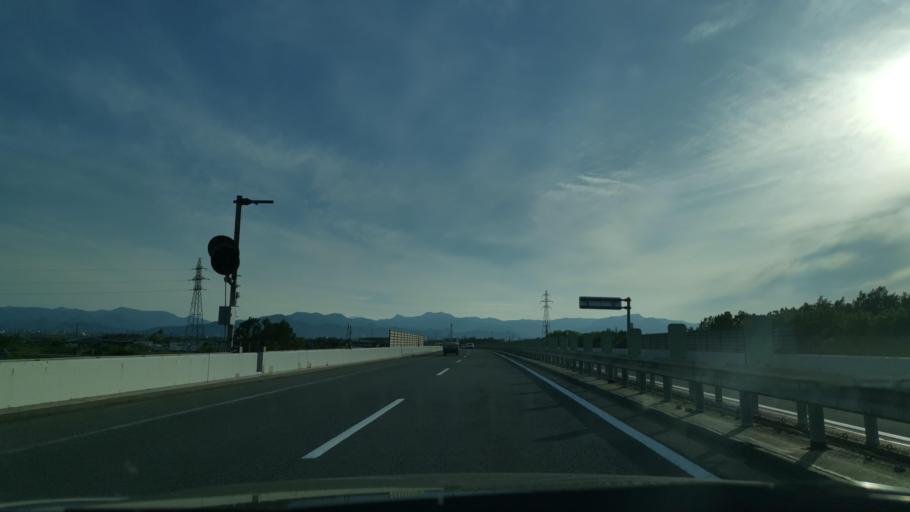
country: JP
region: Hokkaido
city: Ebetsu
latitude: 43.0924
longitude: 141.4707
